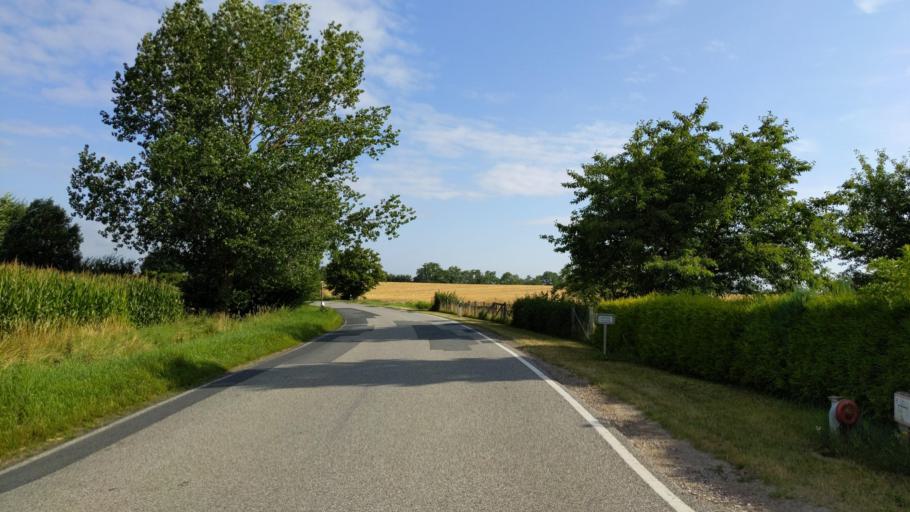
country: DE
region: Schleswig-Holstein
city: Bad Schwartau
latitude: 53.9707
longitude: 10.6560
